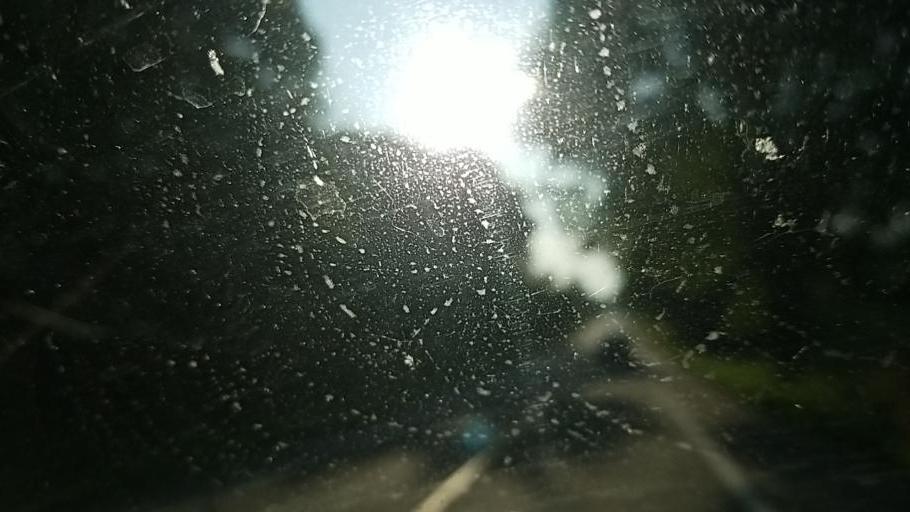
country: US
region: Michigan
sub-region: Montcalm County
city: Stanton
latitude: 43.2500
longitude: -85.1121
